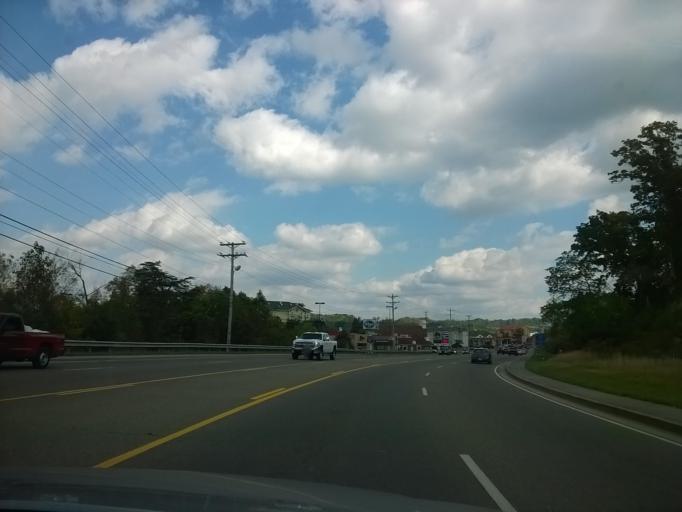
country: US
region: Tennessee
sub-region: Sevier County
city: Pigeon Forge
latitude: 35.8031
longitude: -83.5824
